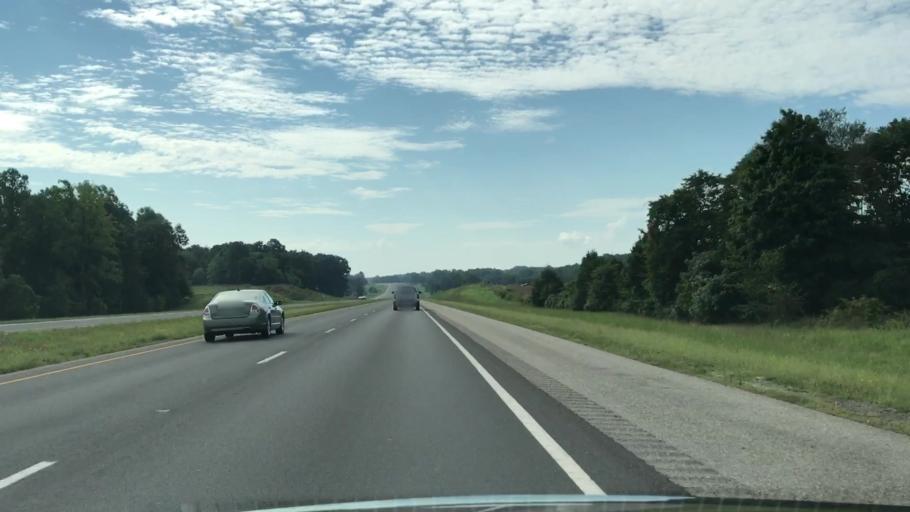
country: US
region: Kentucky
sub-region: Warren County
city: Plano
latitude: 36.8188
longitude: -86.3085
